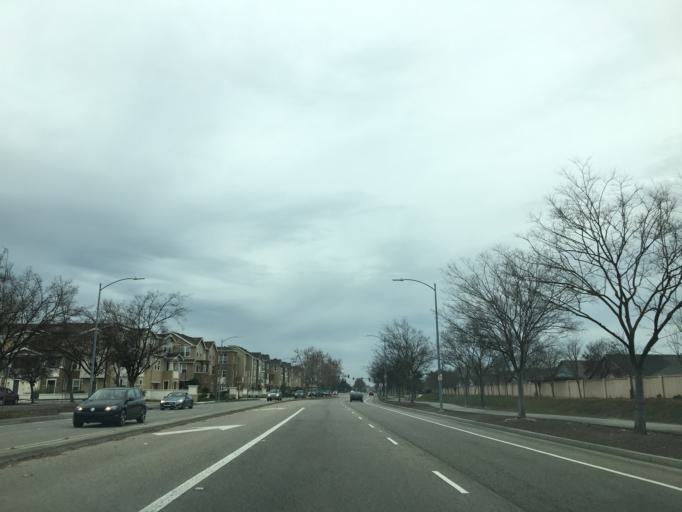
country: US
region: California
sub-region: Santa Clara County
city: Morgan Hill
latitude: 37.1308
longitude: -121.6492
